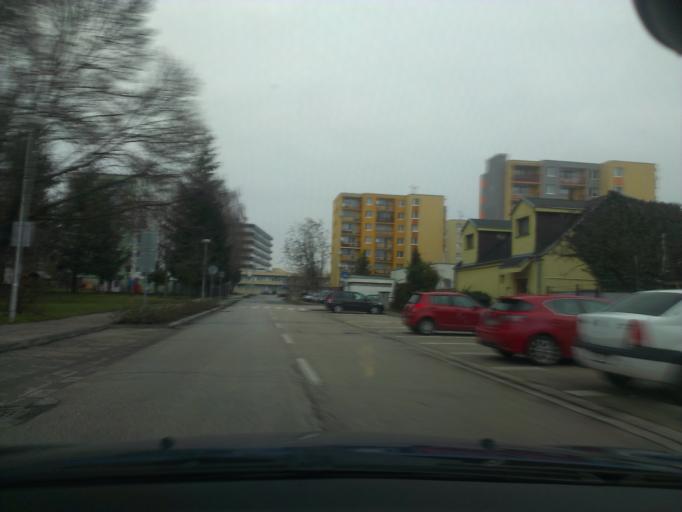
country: SK
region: Trnavsky
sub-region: Okres Trnava
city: Piestany
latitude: 48.5852
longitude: 17.8212
